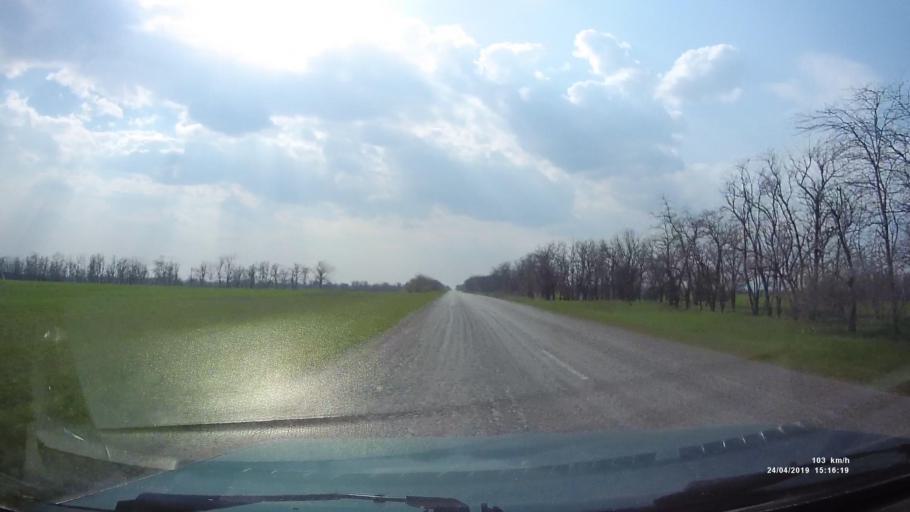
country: RU
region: Rostov
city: Remontnoye
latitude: 46.5465
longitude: 43.2154
